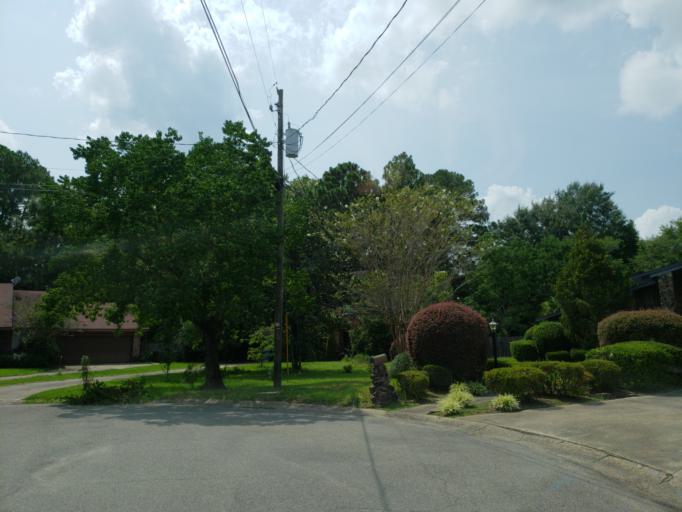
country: US
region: Mississippi
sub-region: Lamar County
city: West Hattiesburg
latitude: 31.3088
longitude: -89.3378
